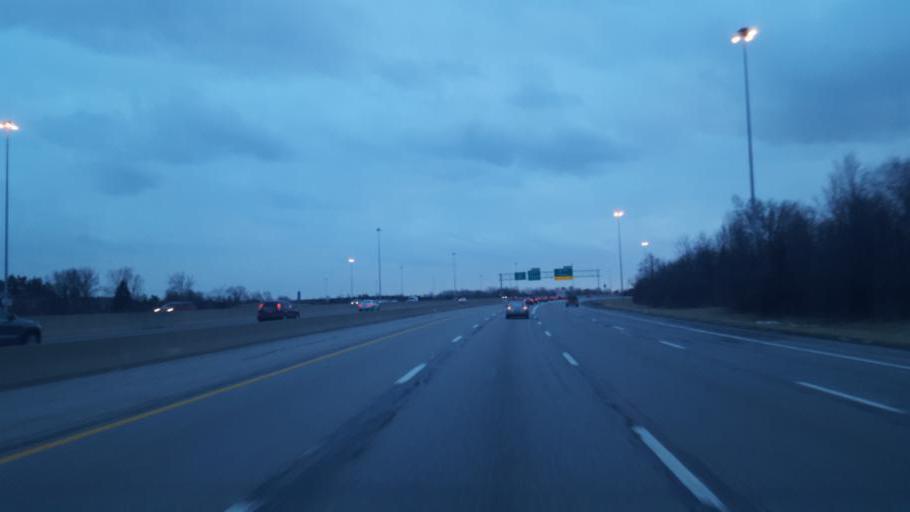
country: US
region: Ohio
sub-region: Franklin County
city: Reynoldsburg
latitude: 39.9404
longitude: -82.8478
